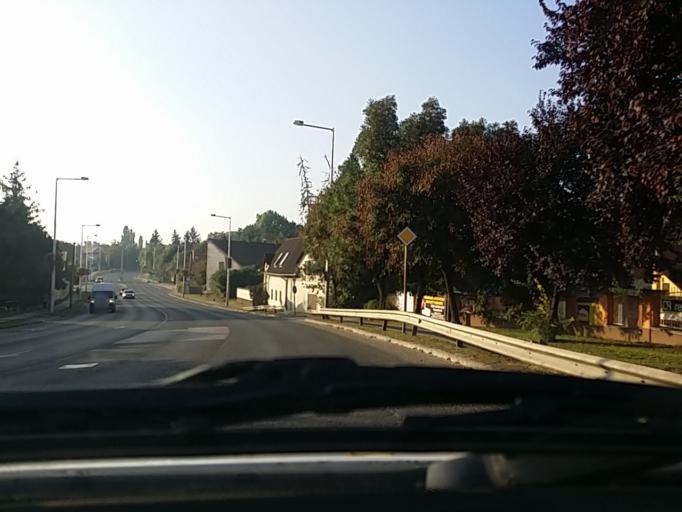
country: HU
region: Pest
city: Szentendre
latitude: 47.6693
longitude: 19.0713
